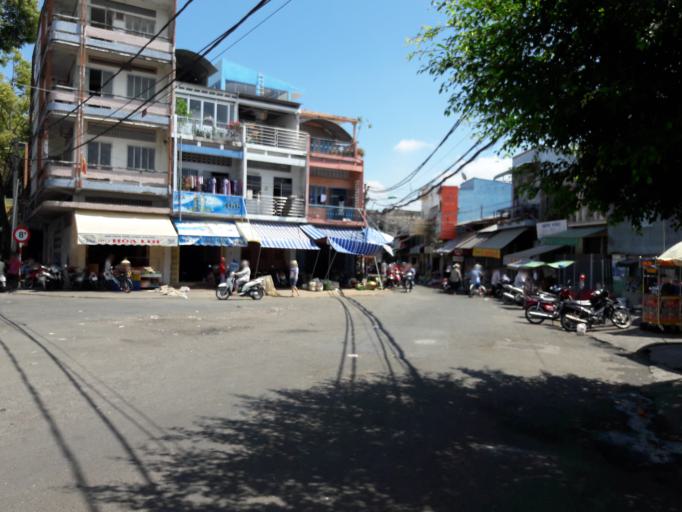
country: VN
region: Can Tho
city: Can Tho
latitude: 10.0270
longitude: 105.7862
